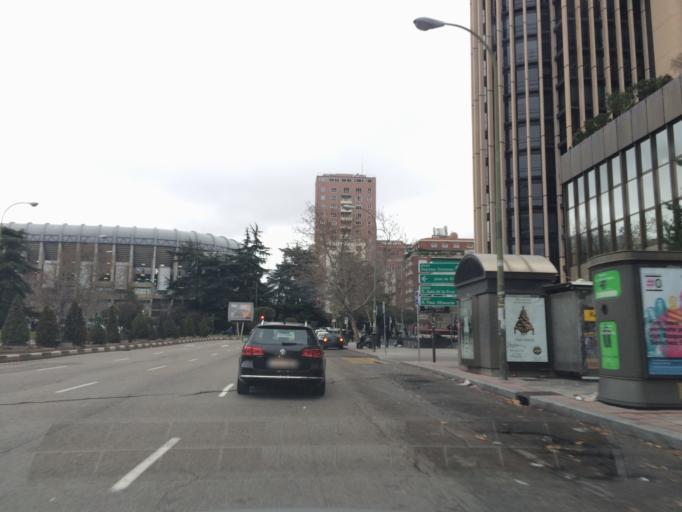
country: ES
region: Madrid
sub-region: Provincia de Madrid
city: Chamartin
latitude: 40.4521
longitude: -3.6926
